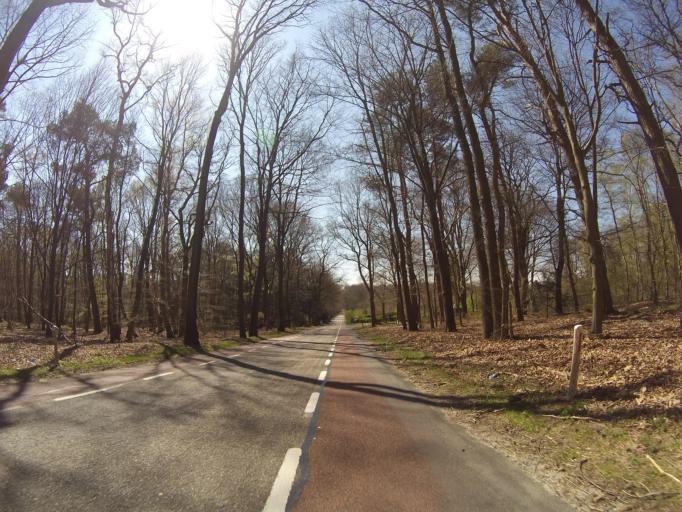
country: NL
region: Utrecht
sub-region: Gemeente Utrechtse Heuvelrug
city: Amerongen
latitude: 52.0135
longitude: 5.4716
